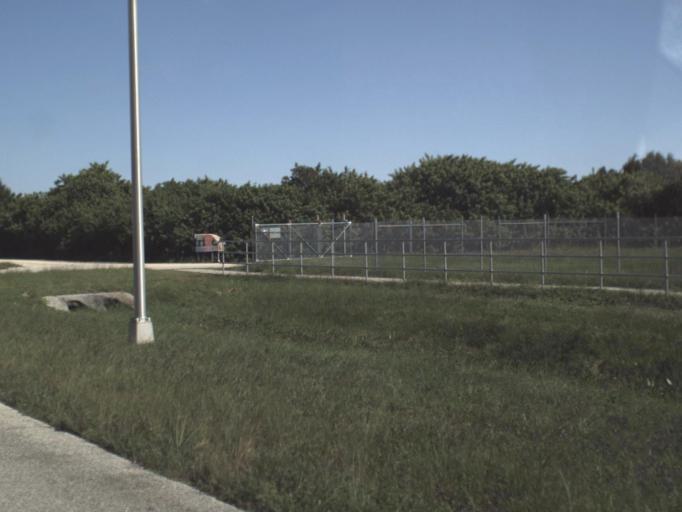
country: US
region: Florida
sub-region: Charlotte County
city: Rotonda
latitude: 26.9329
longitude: -82.2319
